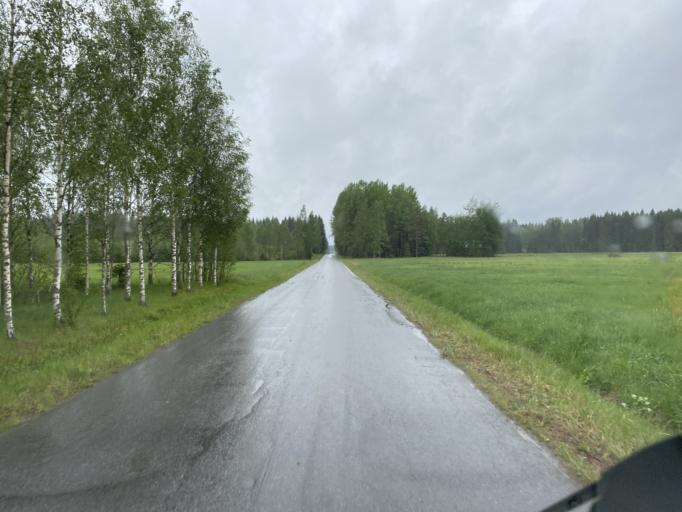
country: FI
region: Haeme
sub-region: Forssa
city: Humppila
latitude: 61.0634
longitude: 23.3241
